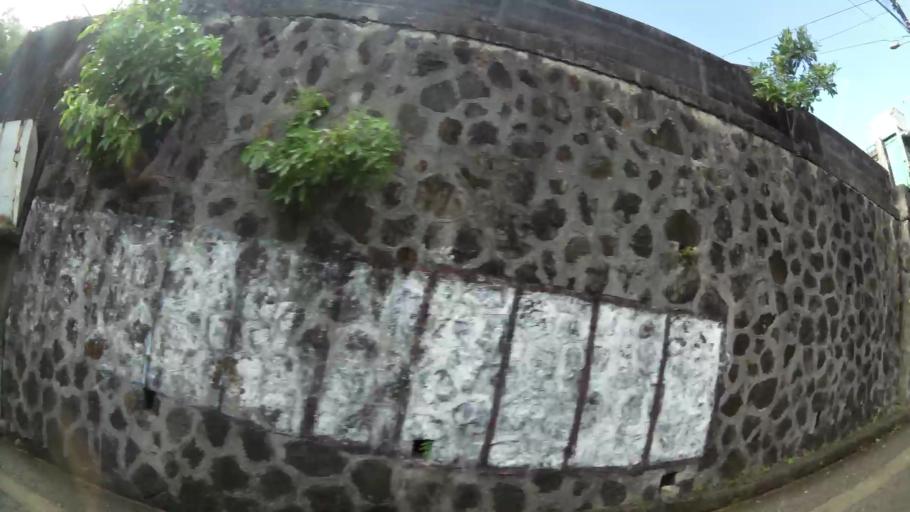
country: MQ
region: Martinique
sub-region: Martinique
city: Fort-de-France
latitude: 14.6136
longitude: -61.0656
